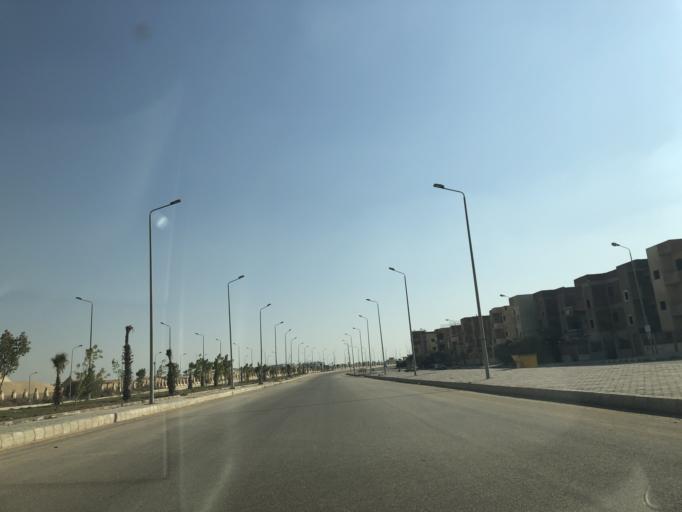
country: EG
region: Al Jizah
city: Madinat Sittah Uktubar
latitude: 29.9325
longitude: 31.0671
